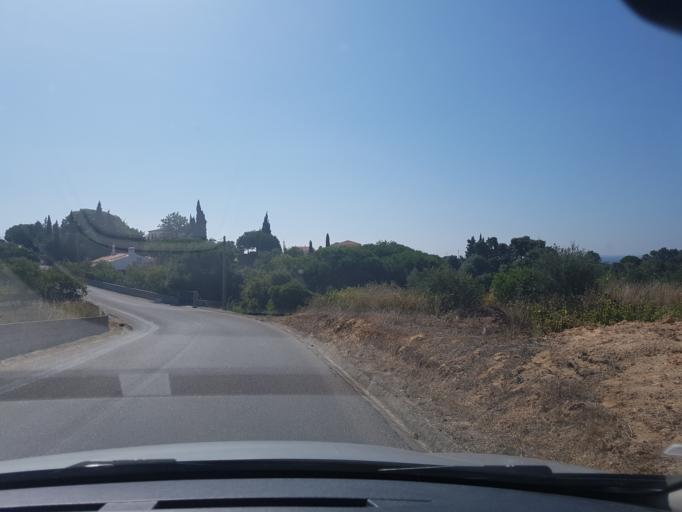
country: PT
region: Faro
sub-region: Lagoa
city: Carvoeiro
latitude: 37.0976
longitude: -8.4215
